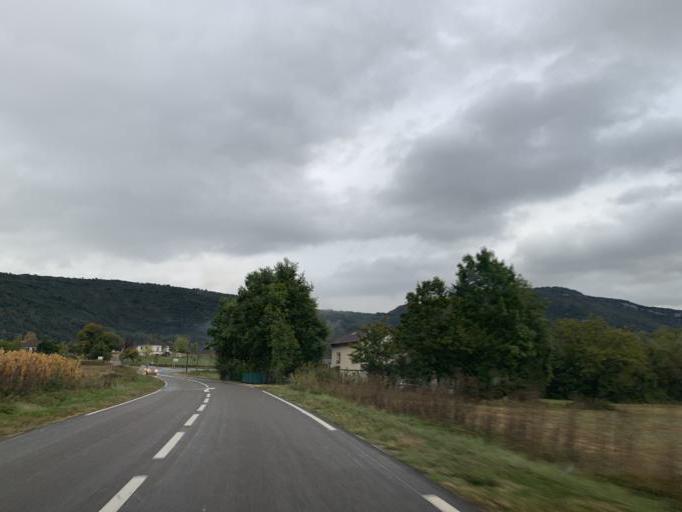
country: FR
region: Rhone-Alpes
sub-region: Departement de l'Isere
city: Les Avenieres
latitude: 45.7080
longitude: 5.5690
